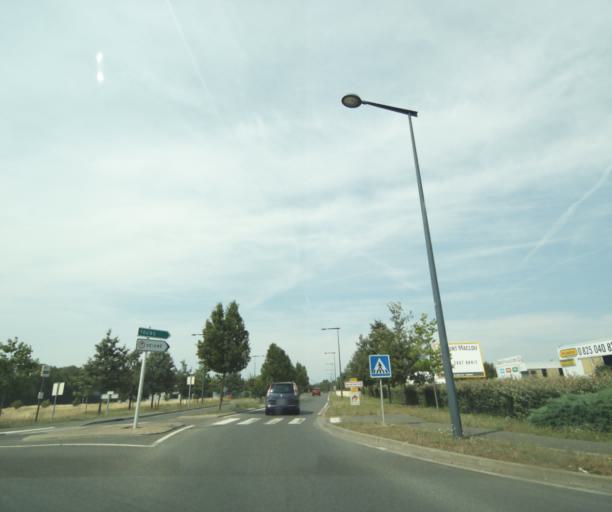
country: FR
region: Centre
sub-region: Departement d'Indre-et-Loire
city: Montbazon
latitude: 47.2748
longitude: 0.7090
